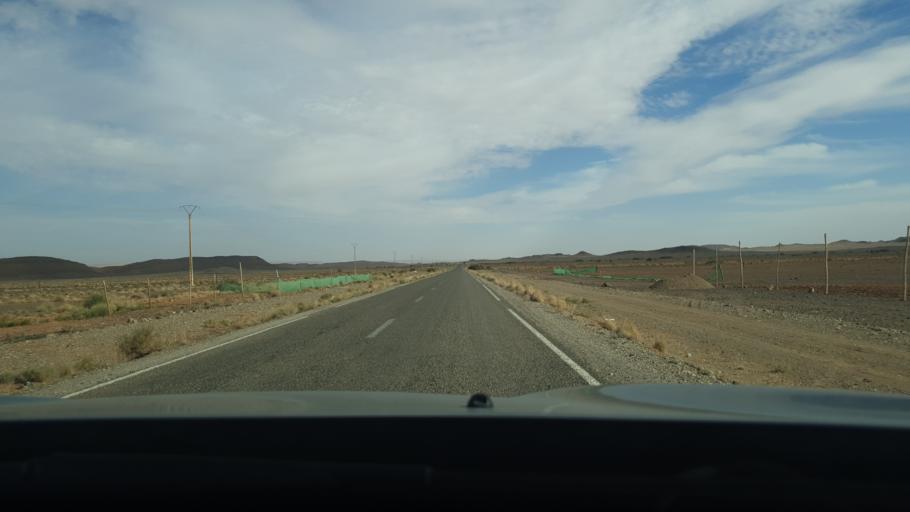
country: MA
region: Meknes-Tafilalet
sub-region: Errachidia
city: Goulmima
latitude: 31.5689
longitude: -4.8108
